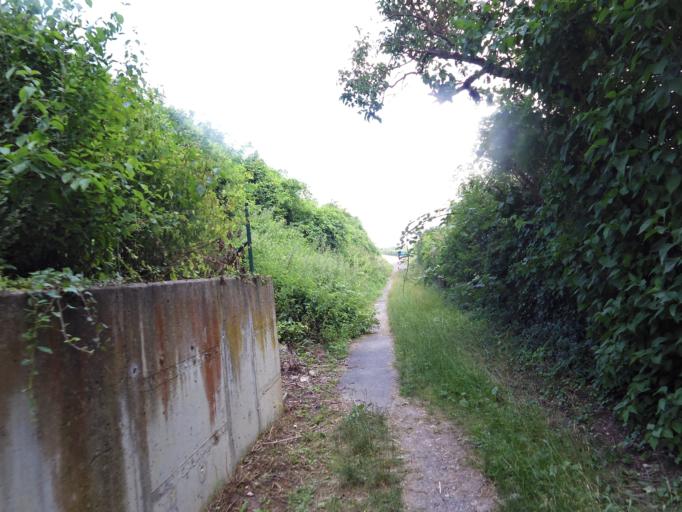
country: DE
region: Bavaria
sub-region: Regierungsbezirk Unterfranken
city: Hochberg
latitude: 49.8068
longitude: 9.8963
